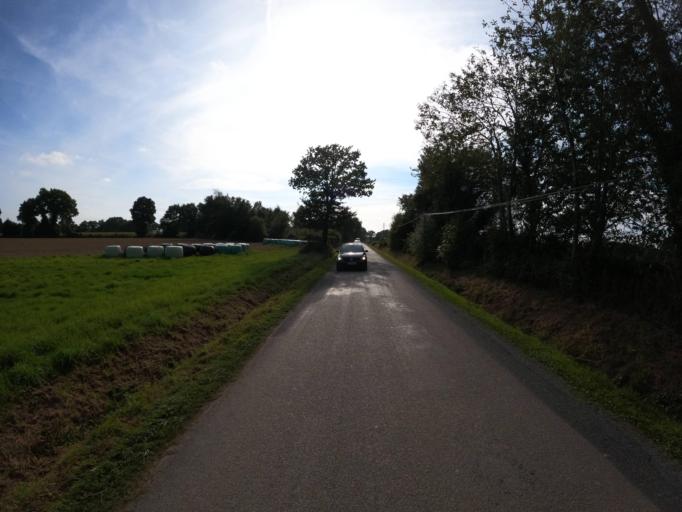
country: FR
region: Brittany
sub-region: Departement du Morbihan
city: Ploermel
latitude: 47.8738
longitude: -2.4057
